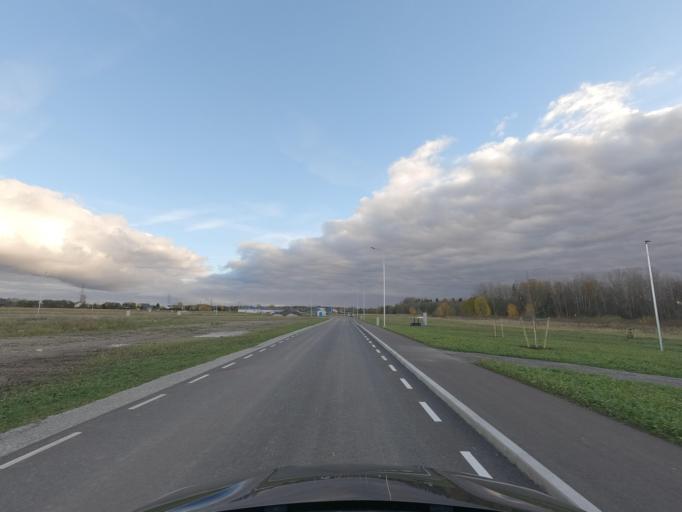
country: EE
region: Harju
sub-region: Saue linn
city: Saue
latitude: 59.3661
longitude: 24.5679
